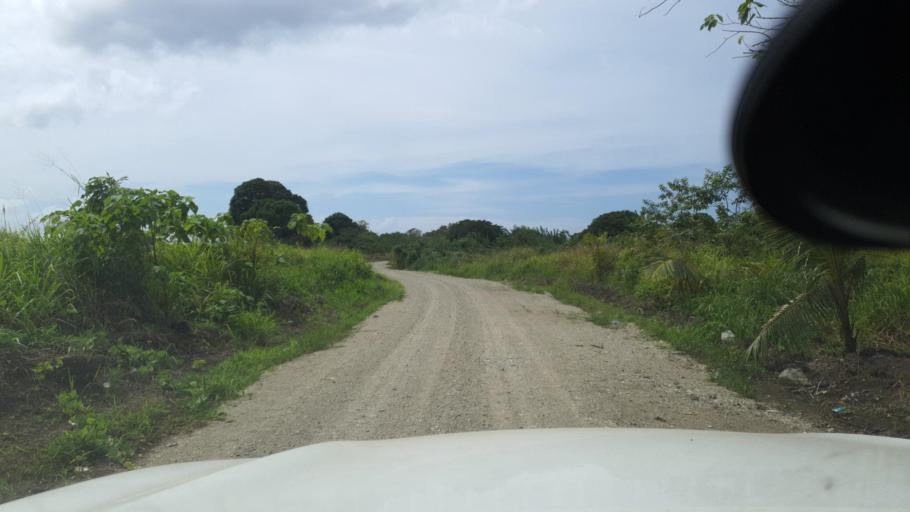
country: SB
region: Guadalcanal
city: Honiara
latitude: -9.4175
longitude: 159.8870
